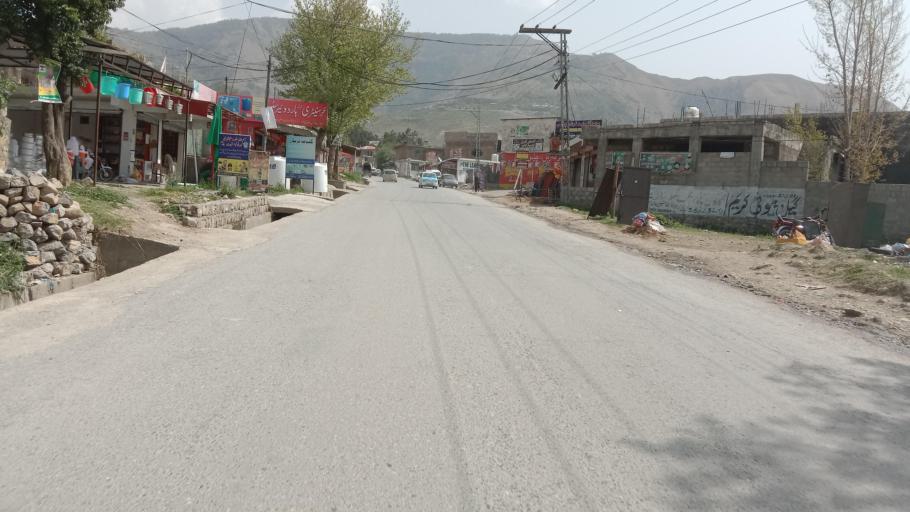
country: PK
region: Khyber Pakhtunkhwa
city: Abbottabad
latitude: 34.1401
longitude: 73.2738
